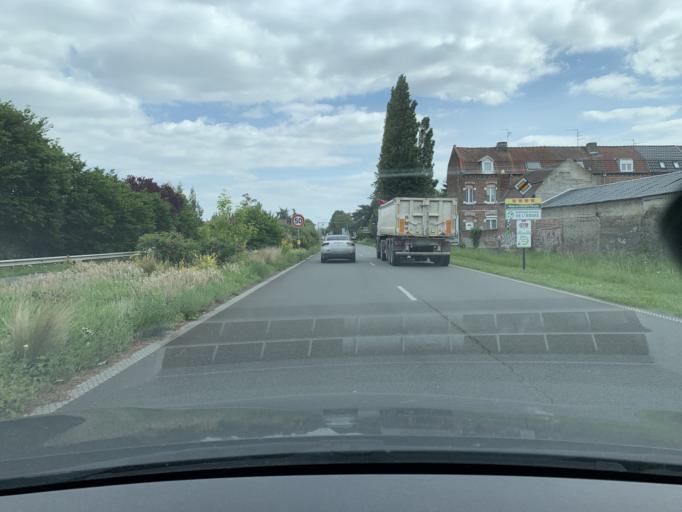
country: FR
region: Nord-Pas-de-Calais
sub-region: Departement du Nord
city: Cuincy
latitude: 50.3774
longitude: 3.0612
